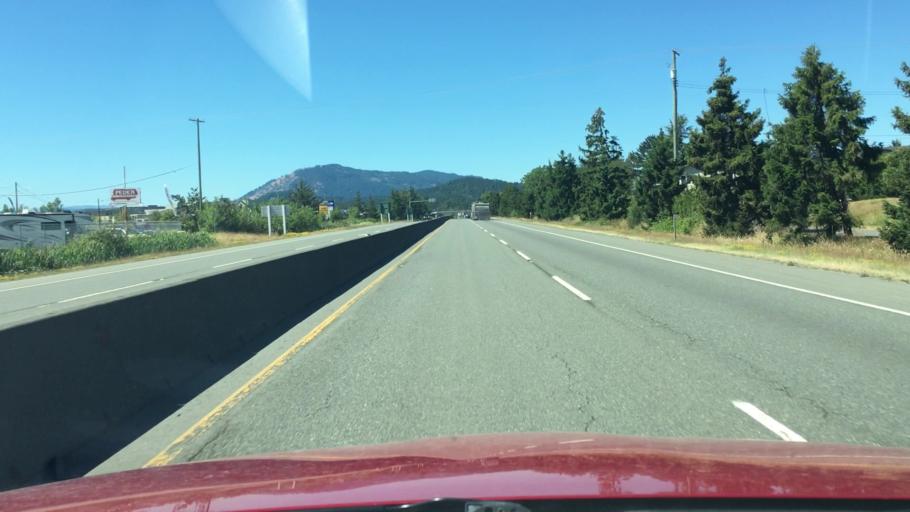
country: CA
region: British Columbia
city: North Saanich
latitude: 48.6547
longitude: -123.4113
